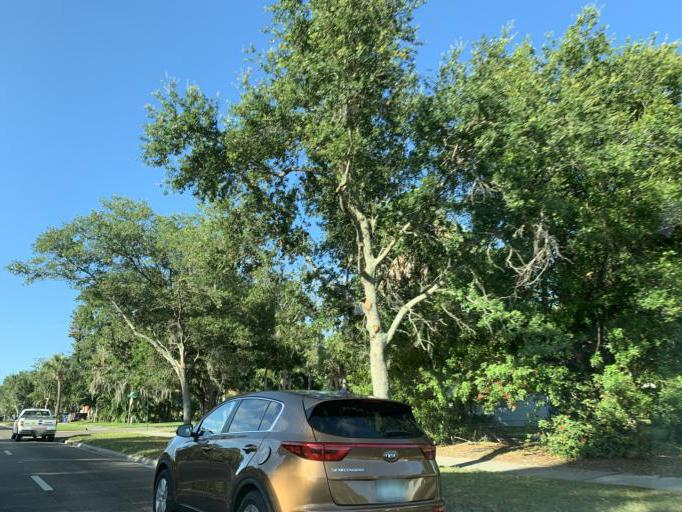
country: US
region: Florida
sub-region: Pinellas County
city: Saint Petersburg
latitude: 27.7436
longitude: -82.6466
